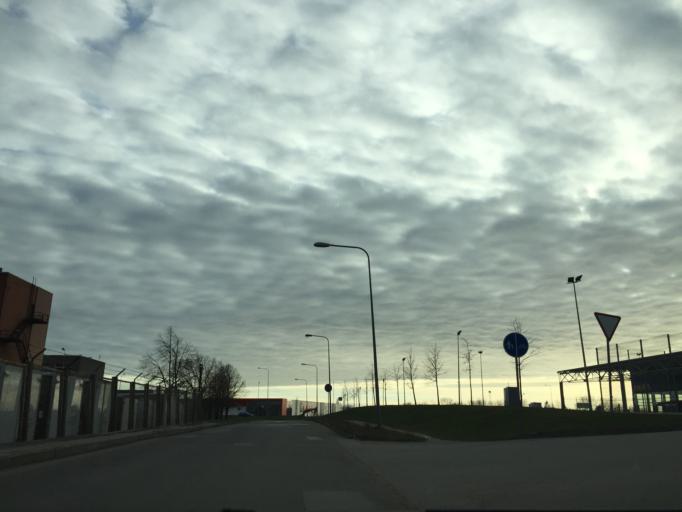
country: LT
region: Klaipedos apskritis
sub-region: Klaipeda
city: Klaipeda
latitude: 55.6966
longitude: 21.1759
